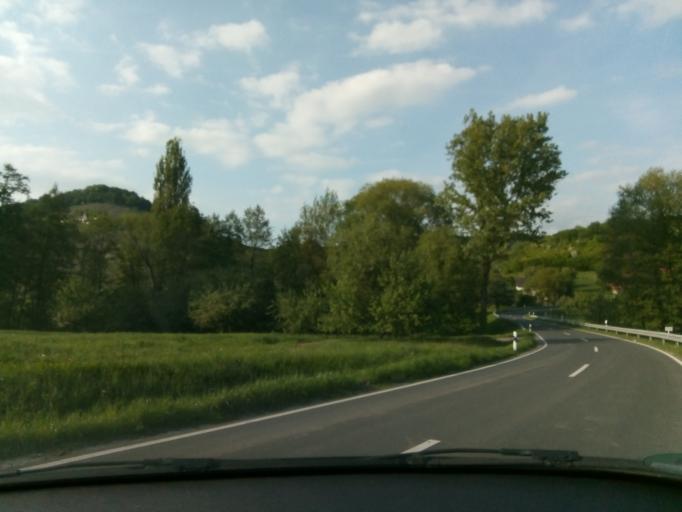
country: DE
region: Bavaria
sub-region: Regierungsbezirk Unterfranken
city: Oberschwarzach
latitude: 49.8684
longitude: 10.4326
